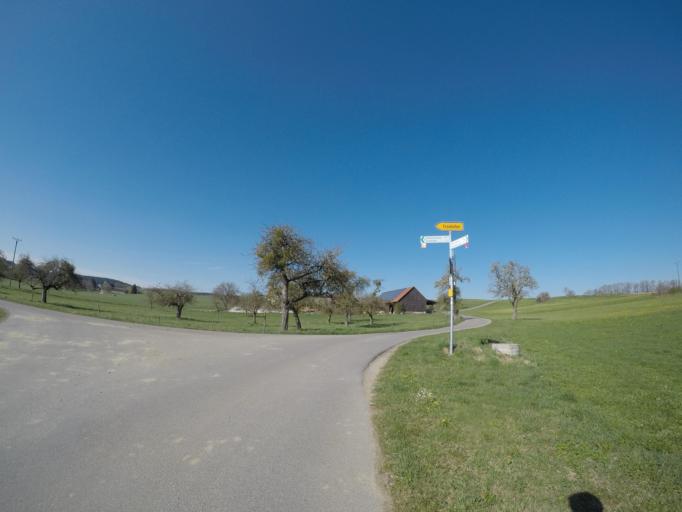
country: DE
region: Baden-Wuerttemberg
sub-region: Tuebingen Region
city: Ebenweiler
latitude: 47.8712
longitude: 9.5103
